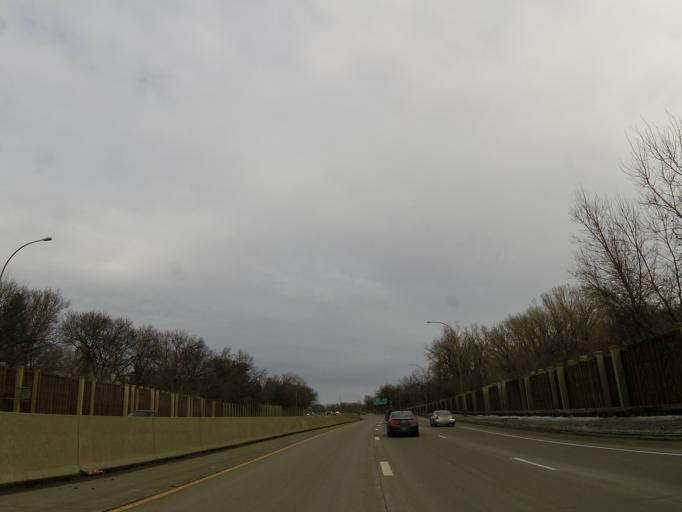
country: US
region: Minnesota
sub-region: Hennepin County
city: Richfield
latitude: 44.8779
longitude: -93.2977
